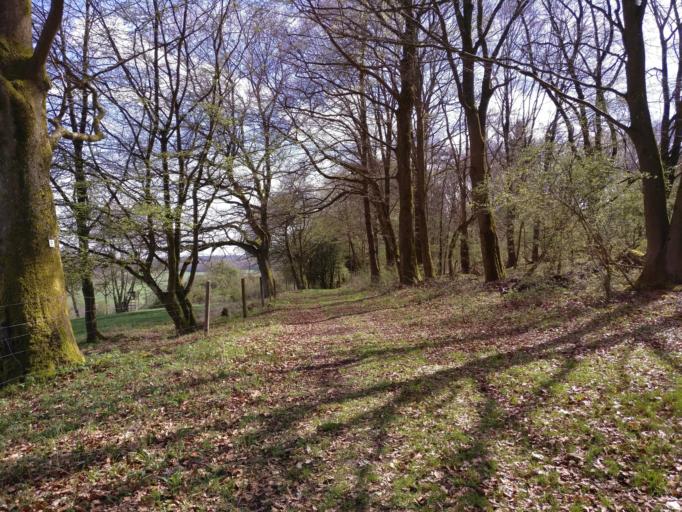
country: DE
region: Hesse
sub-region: Regierungsbezirk Giessen
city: Schwalmtal
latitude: 50.6528
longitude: 9.2431
